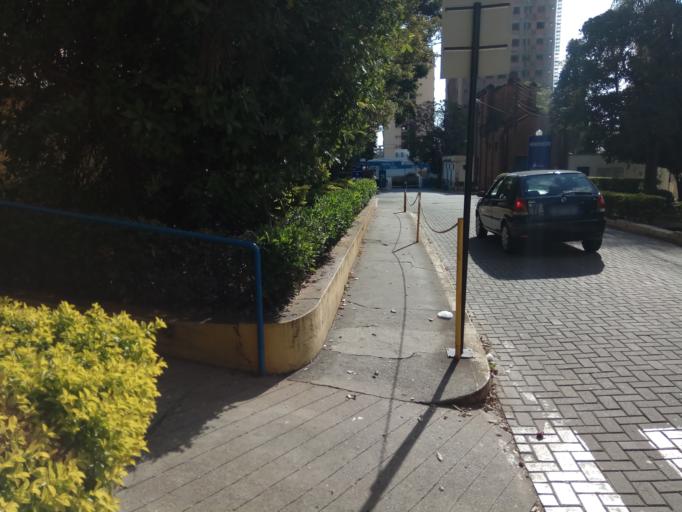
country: BR
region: Sao Paulo
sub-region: Piracicaba
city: Piracicaba
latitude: -22.7368
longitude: -47.6401
